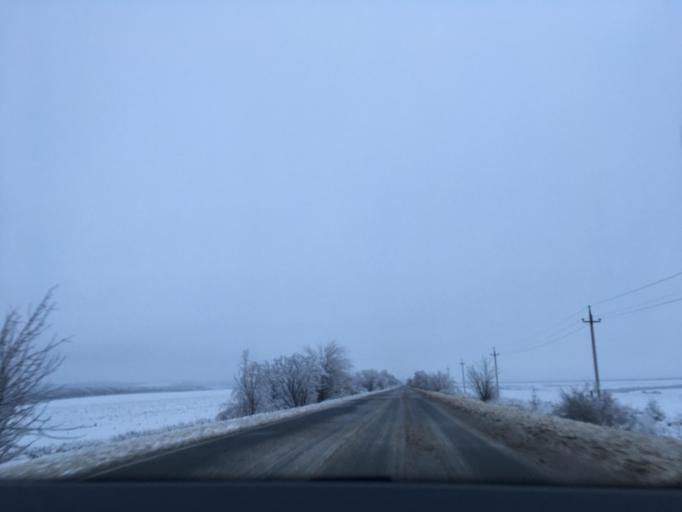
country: RU
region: Voronezj
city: Verkhniy Mamon
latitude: 50.0223
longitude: 40.0902
